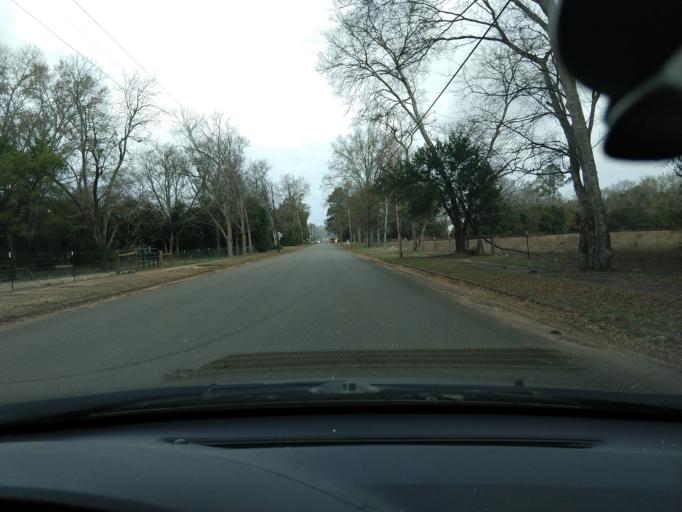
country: US
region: Georgia
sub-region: Calhoun County
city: Edison
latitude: 31.5175
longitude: -84.8651
